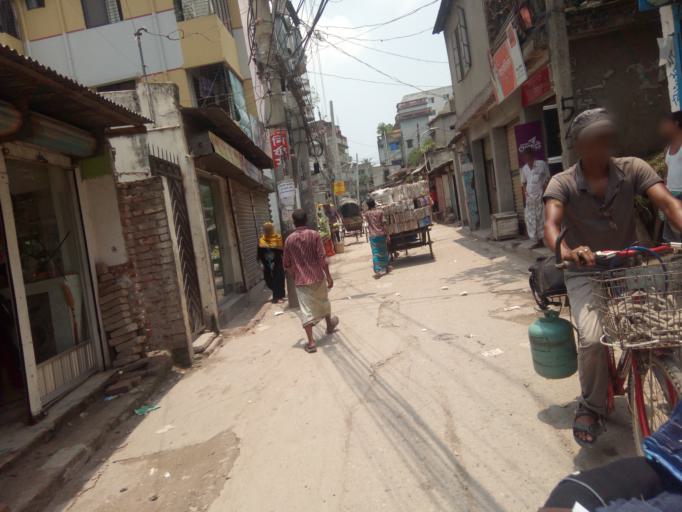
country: BD
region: Dhaka
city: Paltan
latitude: 23.7590
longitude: 90.4326
